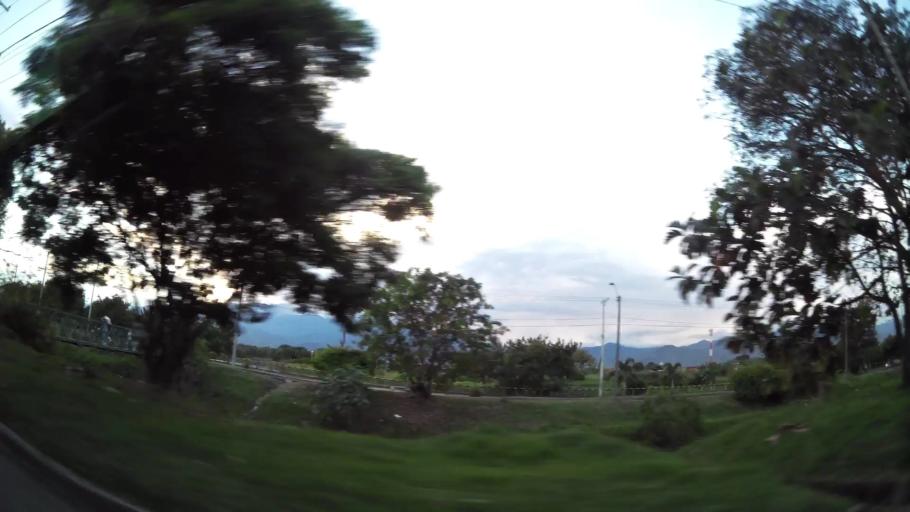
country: CO
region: Valle del Cauca
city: Cali
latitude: 3.4381
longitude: -76.4838
